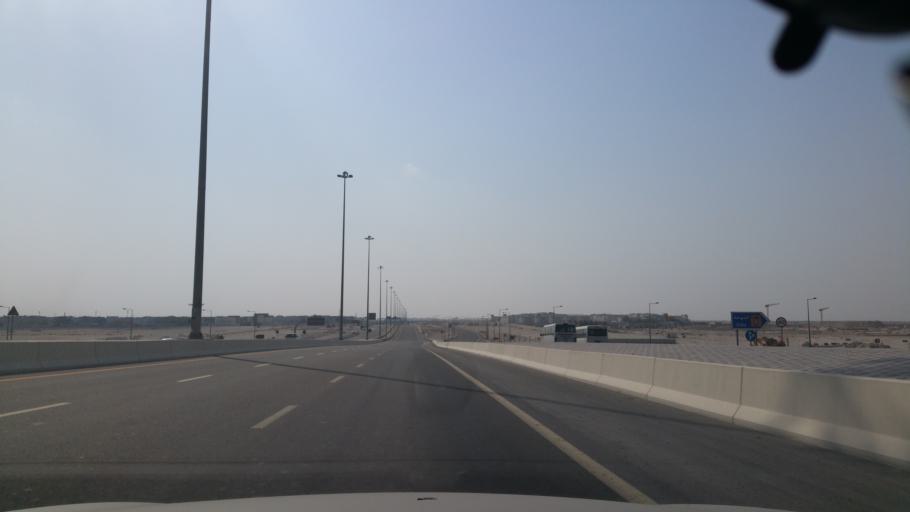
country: QA
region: Baladiyat Umm Salal
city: Umm Salal `Ali
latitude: 25.4571
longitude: 51.4769
